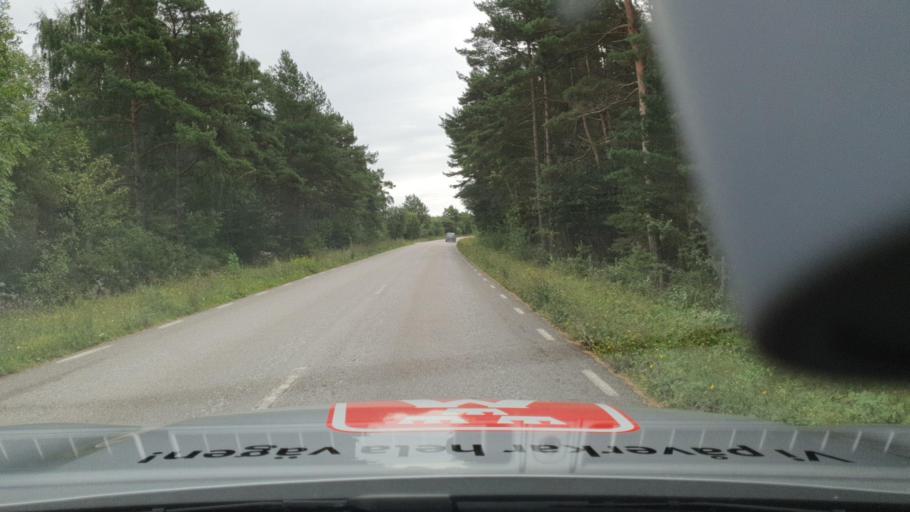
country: SE
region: Gotland
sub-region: Gotland
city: Hemse
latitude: 57.1056
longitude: 18.2968
